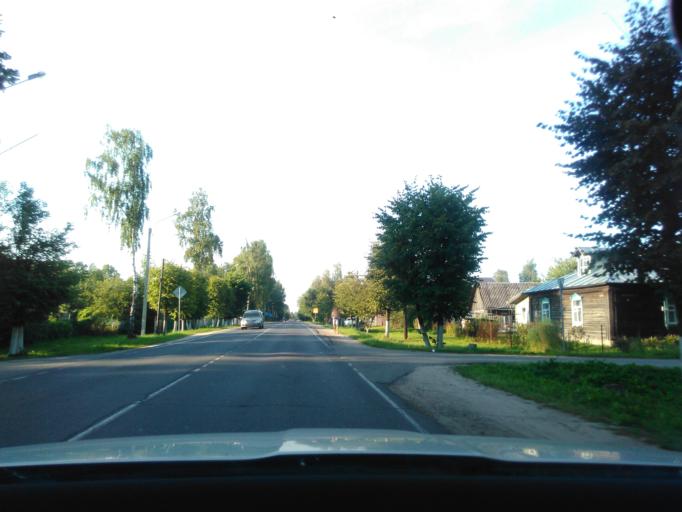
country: RU
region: Tverskaya
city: Konakovo
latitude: 56.6852
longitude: 36.7621
